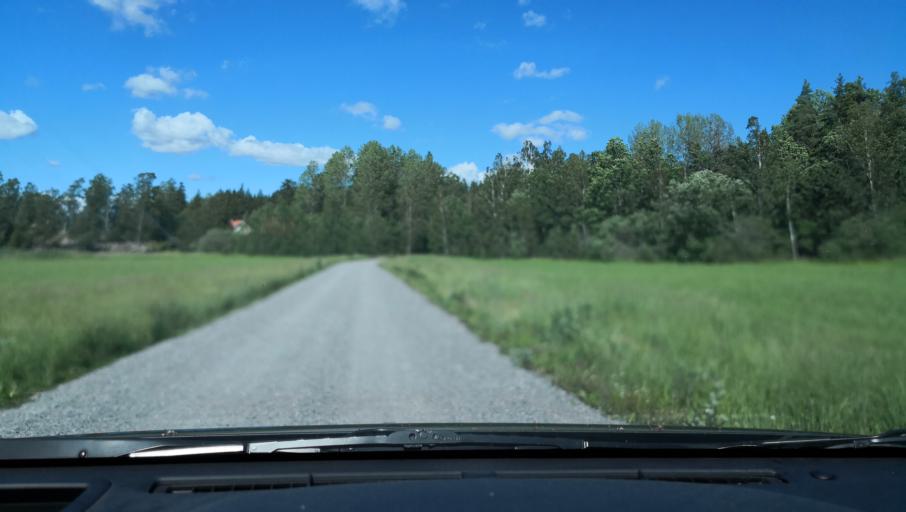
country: SE
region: Soedermanland
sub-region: Eskilstuna Kommun
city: Hallbybrunn
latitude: 59.3063
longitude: 16.3658
